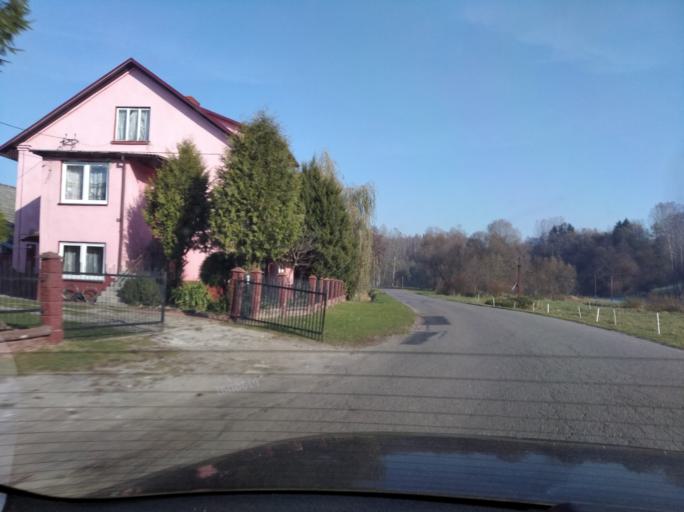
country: PL
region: Subcarpathian Voivodeship
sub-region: Powiat ropczycko-sedziszowski
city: Wielopole Skrzynskie
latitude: 49.9386
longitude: 21.5771
